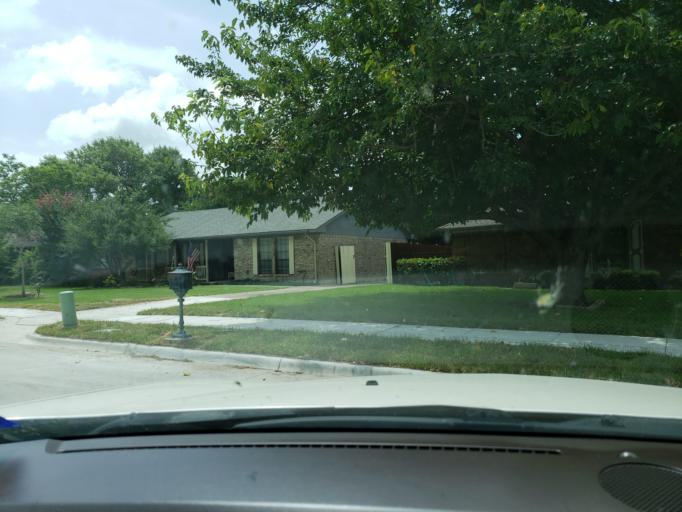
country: US
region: Texas
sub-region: Dallas County
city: Rowlett
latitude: 32.8949
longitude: -96.5641
